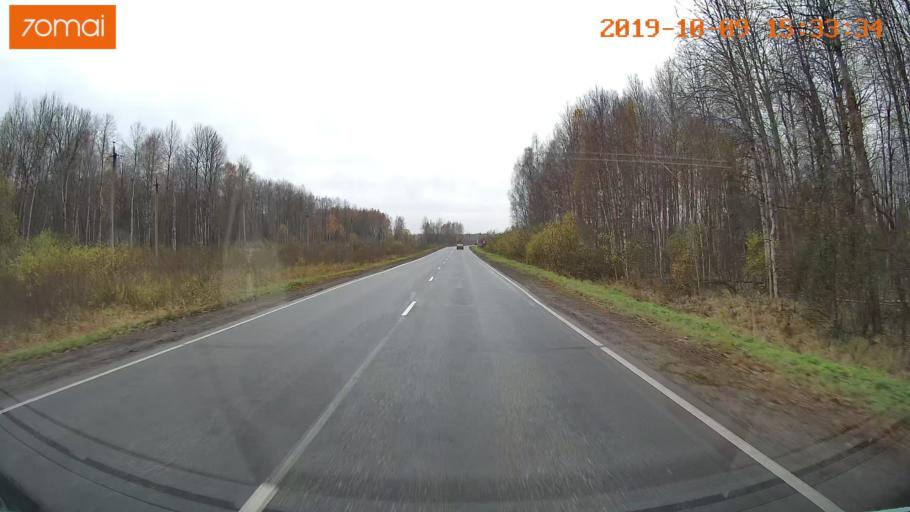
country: RU
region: Kostroma
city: Oktyabr'skiy
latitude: 57.9499
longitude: 41.2606
